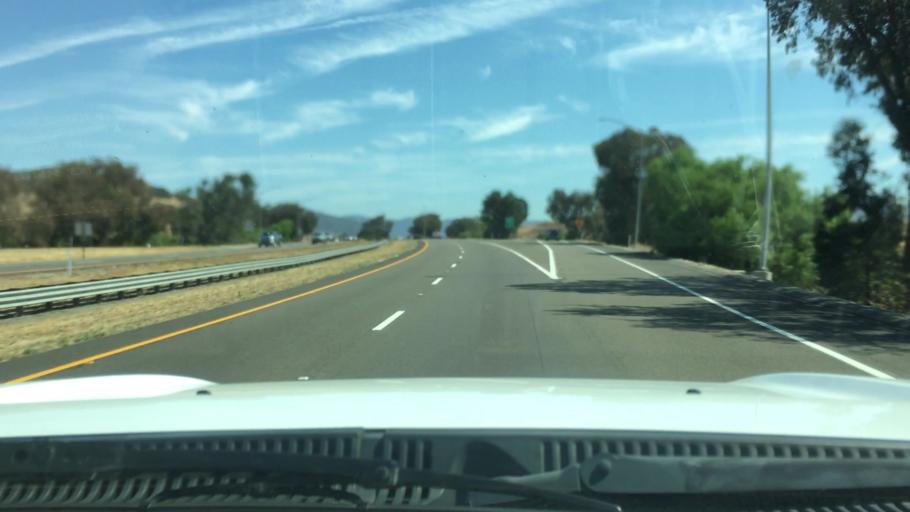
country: US
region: California
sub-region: San Luis Obispo County
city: Avila Beach
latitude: 35.2210
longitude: -120.6921
